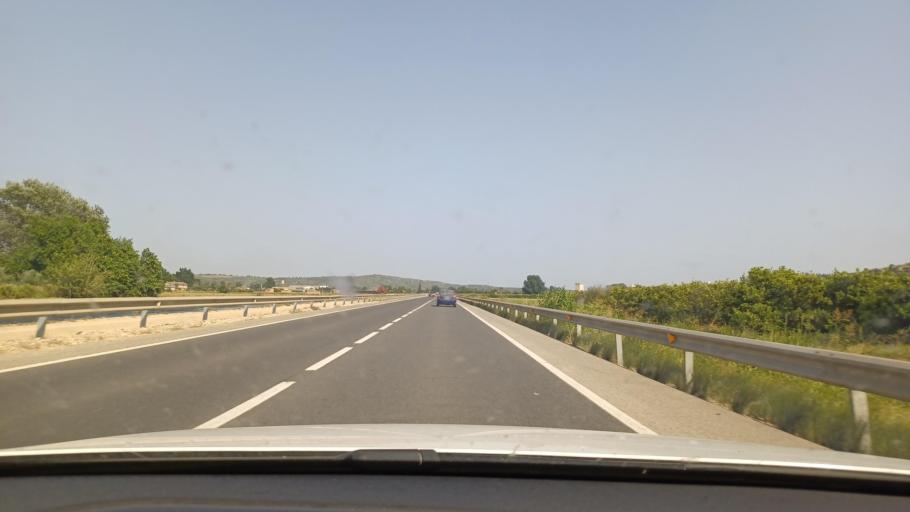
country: ES
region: Catalonia
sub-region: Provincia de Tarragona
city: Masdenverge
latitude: 40.7511
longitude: 0.5470
